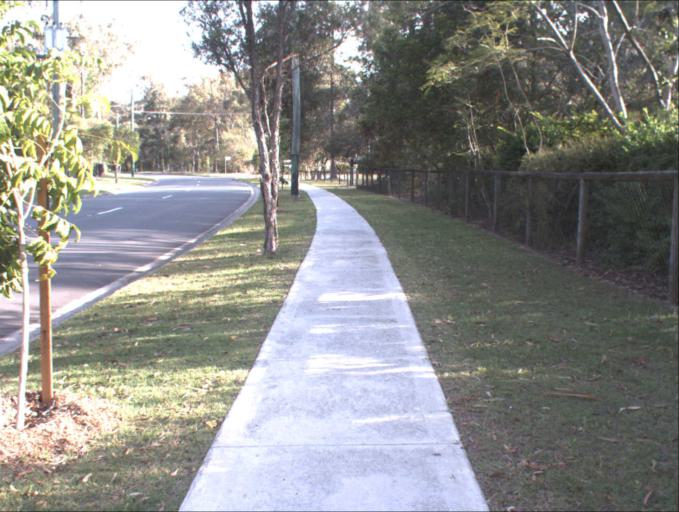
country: AU
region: Queensland
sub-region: Logan
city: Park Ridge South
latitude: -27.6707
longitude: 153.0137
